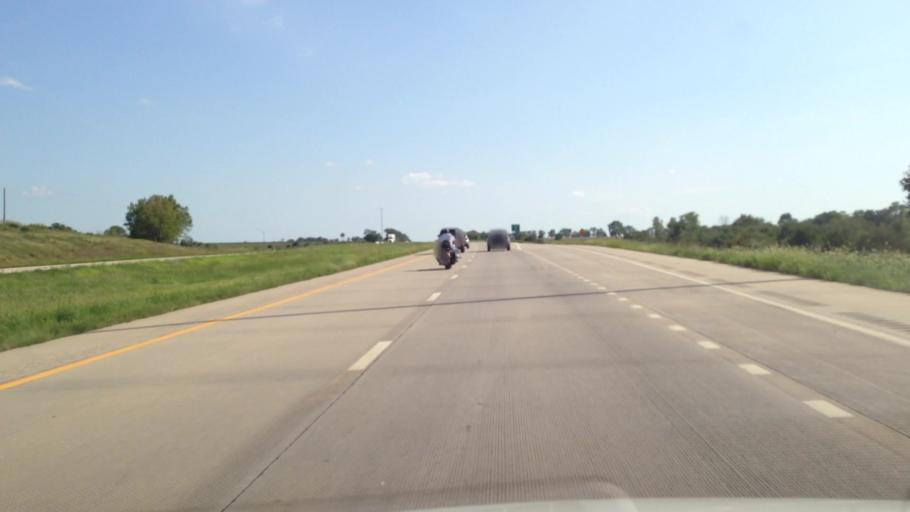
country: US
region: Kansas
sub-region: Bourbon County
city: Fort Scott
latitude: 37.9977
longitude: -94.7051
